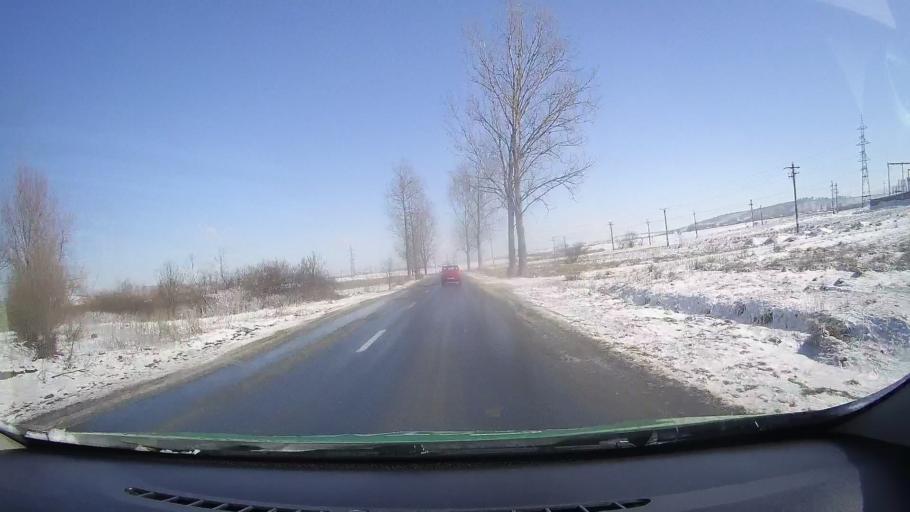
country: RO
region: Sibiu
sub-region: Comuna Avrig
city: Marsa
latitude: 45.7051
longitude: 24.3668
